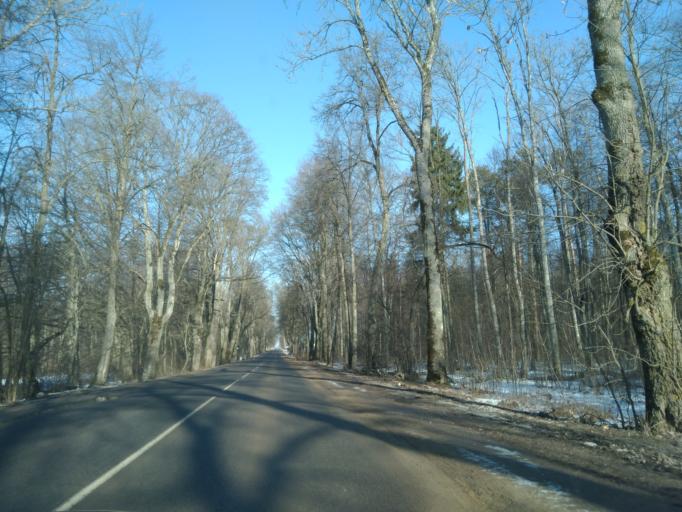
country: BY
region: Minsk
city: Nyasvizh
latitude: 53.2015
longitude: 26.6563
